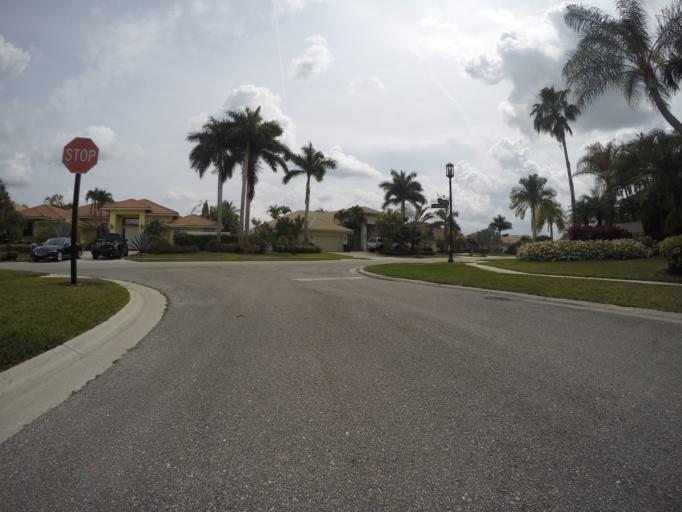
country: US
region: Florida
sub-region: Palm Beach County
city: Villages of Oriole
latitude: 26.4141
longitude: -80.2233
